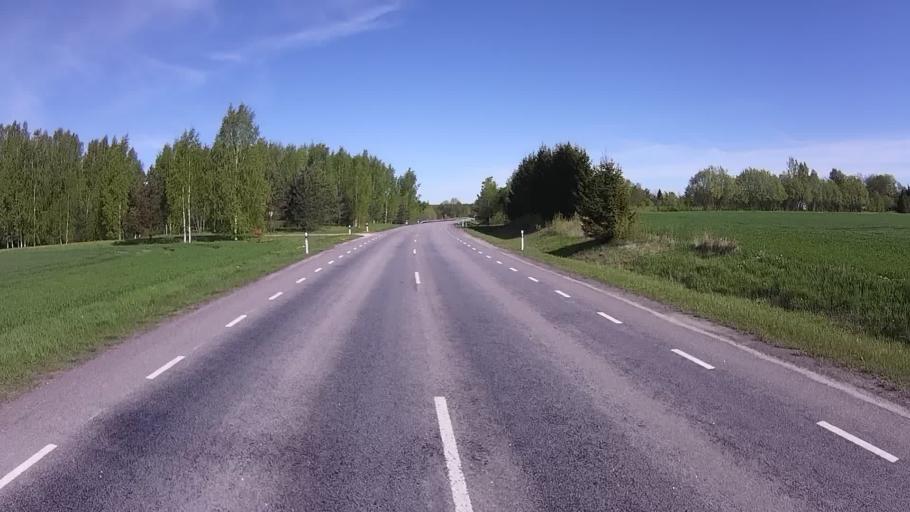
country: EE
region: Polvamaa
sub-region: Polva linn
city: Polva
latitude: 58.2472
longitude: 27.0032
